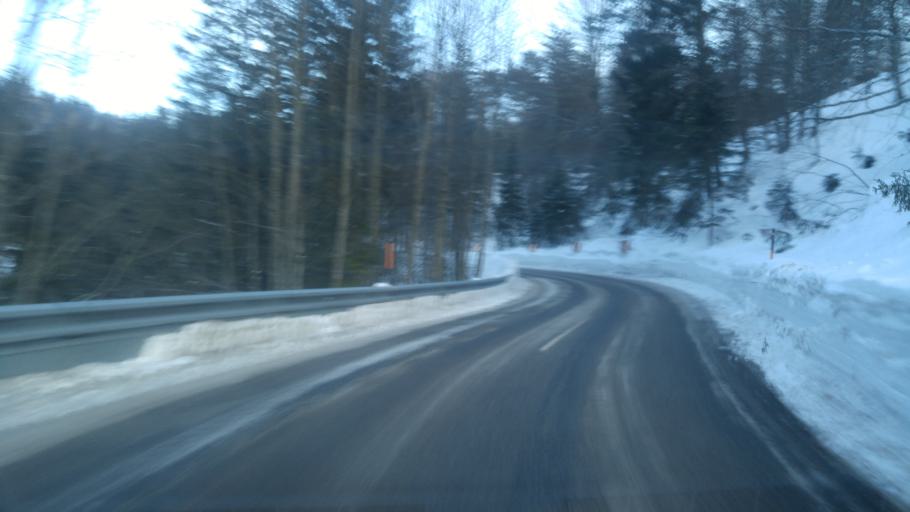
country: AT
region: Lower Austria
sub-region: Politischer Bezirk Lilienfeld
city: Hohenberg
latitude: 47.8899
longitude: 15.6695
